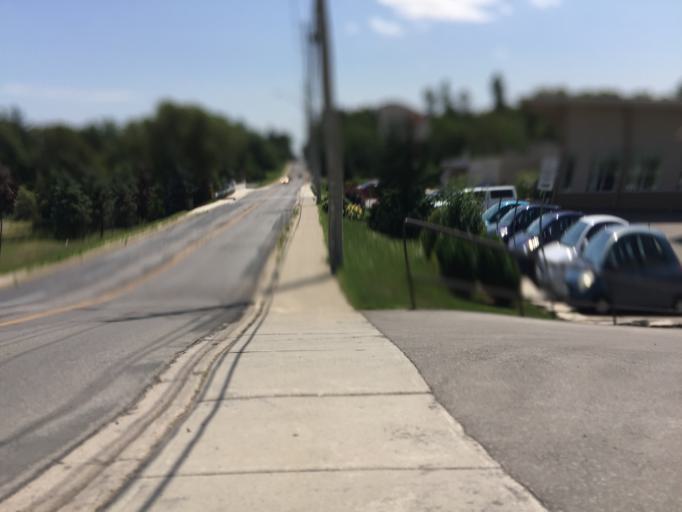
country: CA
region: Ontario
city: Stratford
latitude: 43.3784
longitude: -80.9632
